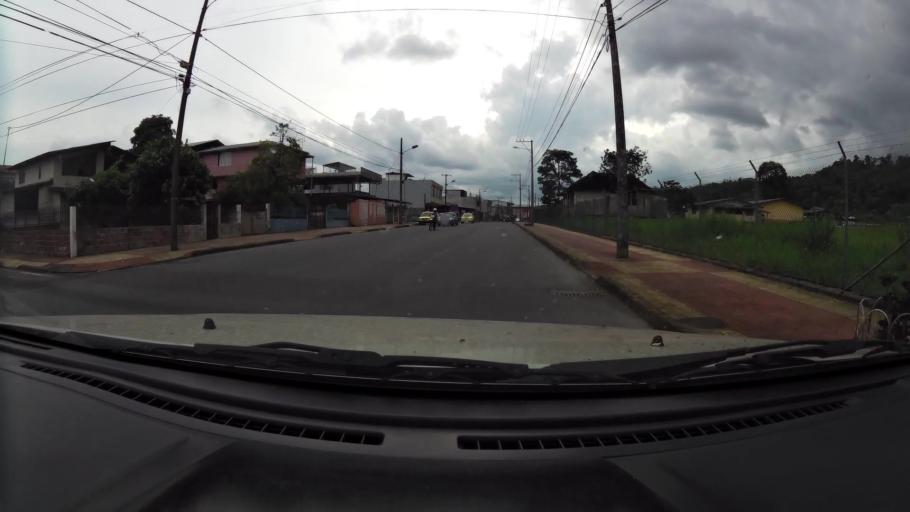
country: EC
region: Pastaza
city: Puyo
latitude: -1.4902
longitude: -78.0125
